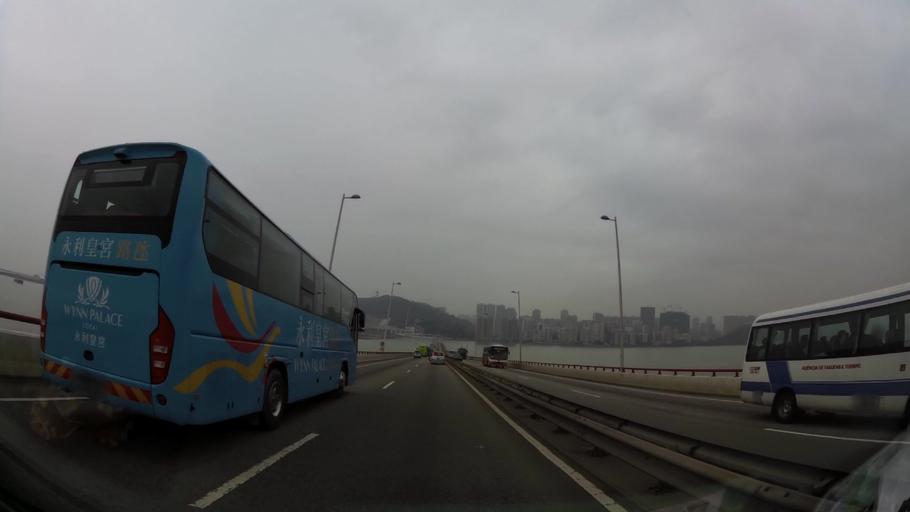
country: MO
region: Macau
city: Macau
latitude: 22.1772
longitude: 113.5635
